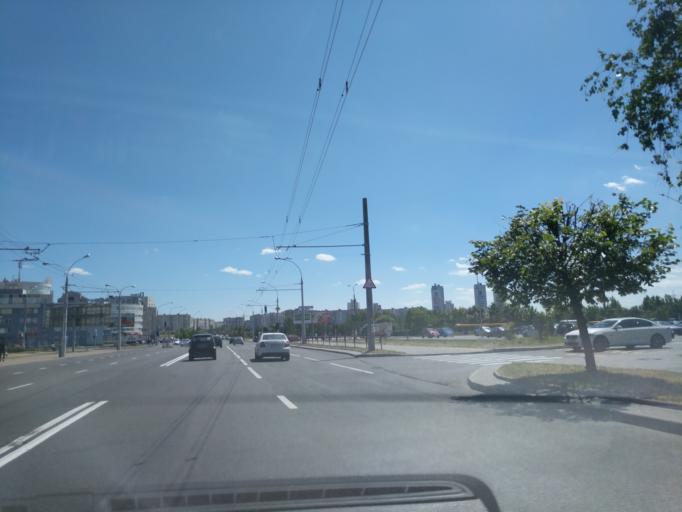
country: BY
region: Minsk
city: Borovlyany
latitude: 53.9485
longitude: 27.6795
